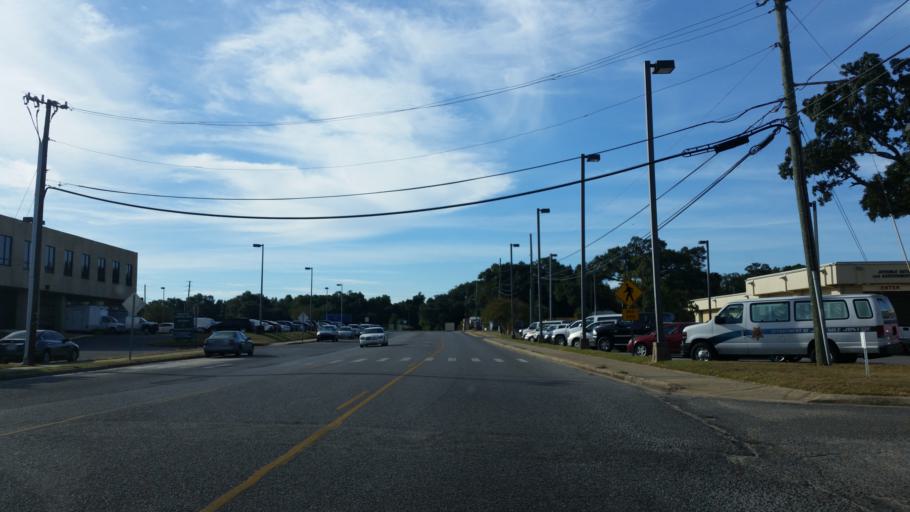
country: US
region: Florida
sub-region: Escambia County
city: Goulding
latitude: 30.4430
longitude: -87.2360
